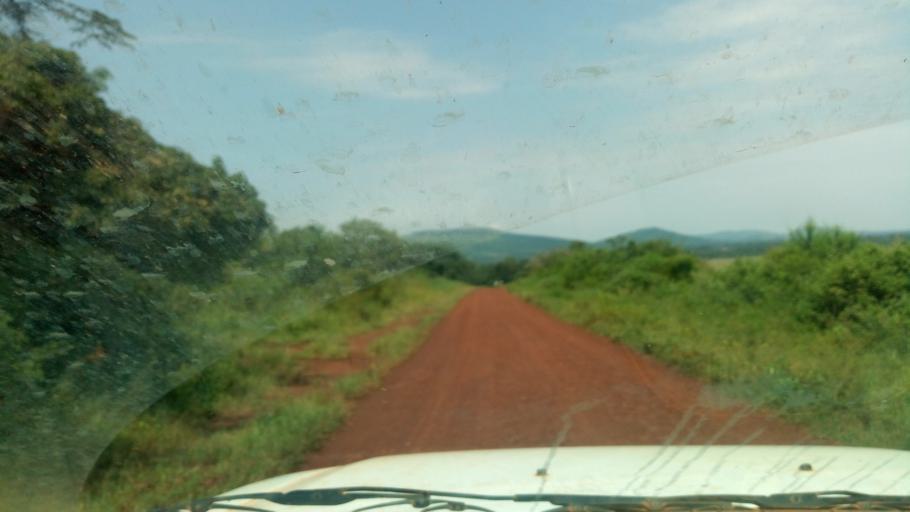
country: UG
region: Western Region
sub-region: Masindi District
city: Masindi
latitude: 1.6651
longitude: 31.8166
